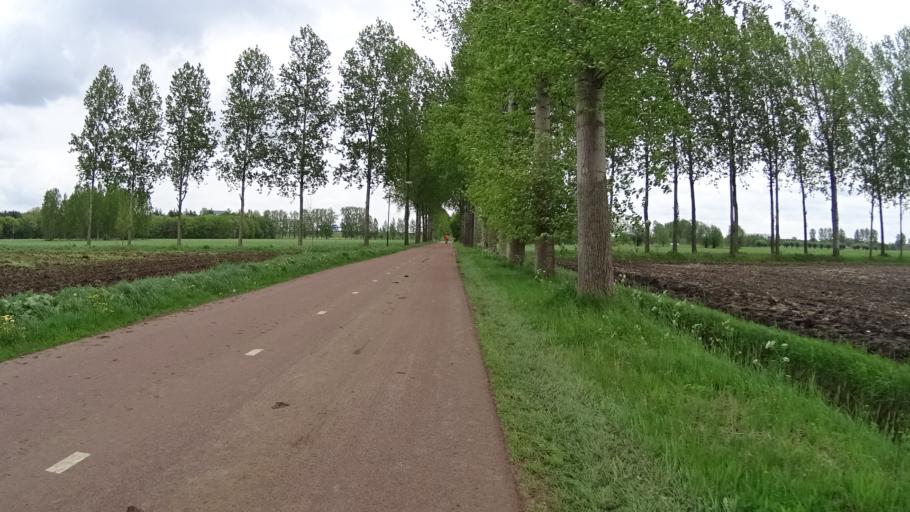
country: NL
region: North Brabant
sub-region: Gemeente Veghel
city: Eerde
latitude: 51.6173
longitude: 5.4911
